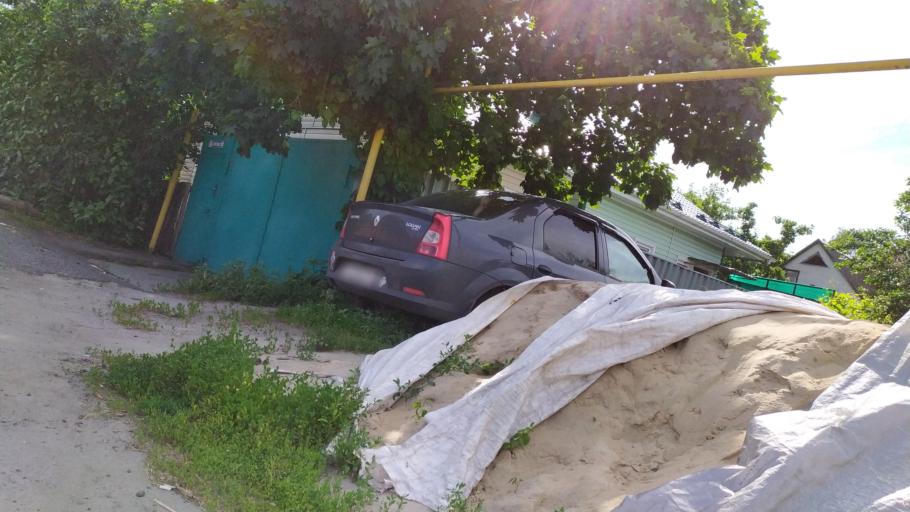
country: RU
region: Kursk
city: Kursk
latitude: 51.6614
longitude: 36.1535
